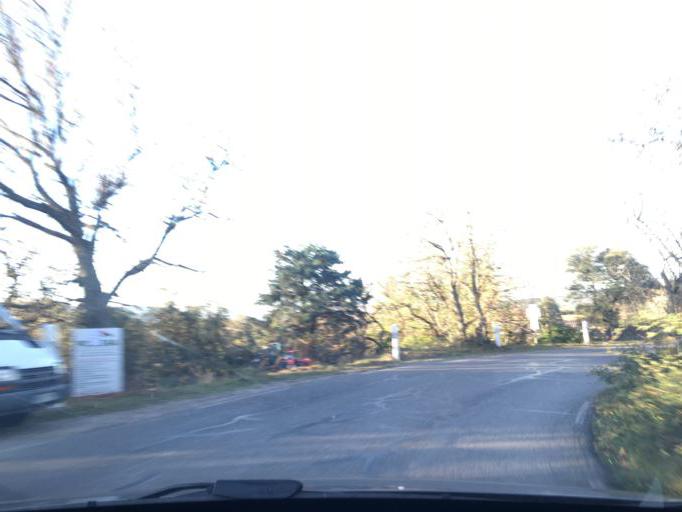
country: FR
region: Provence-Alpes-Cote d'Azur
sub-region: Departement du Vaucluse
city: Gordes
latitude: 43.9045
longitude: 5.1966
